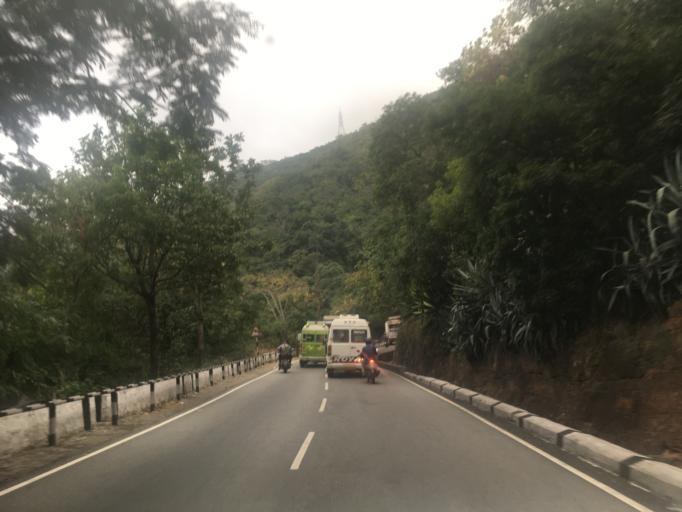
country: IN
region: Andhra Pradesh
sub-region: Chittoor
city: Tirumala
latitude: 13.6646
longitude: 79.3487
